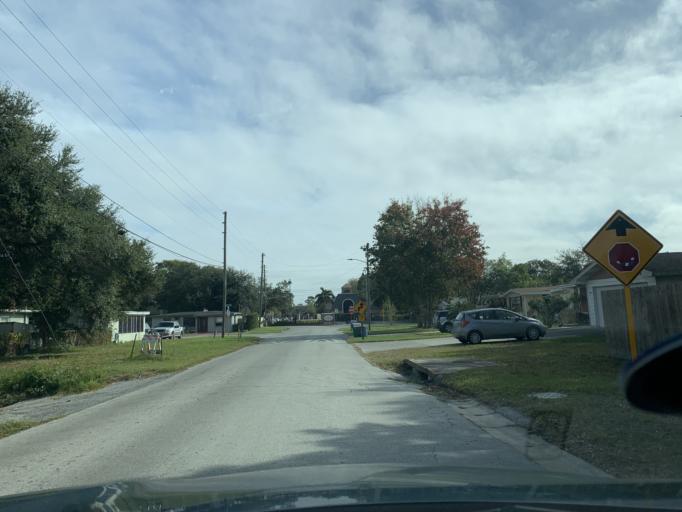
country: US
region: Florida
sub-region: Pinellas County
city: Ridgecrest
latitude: 27.8802
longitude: -82.7819
